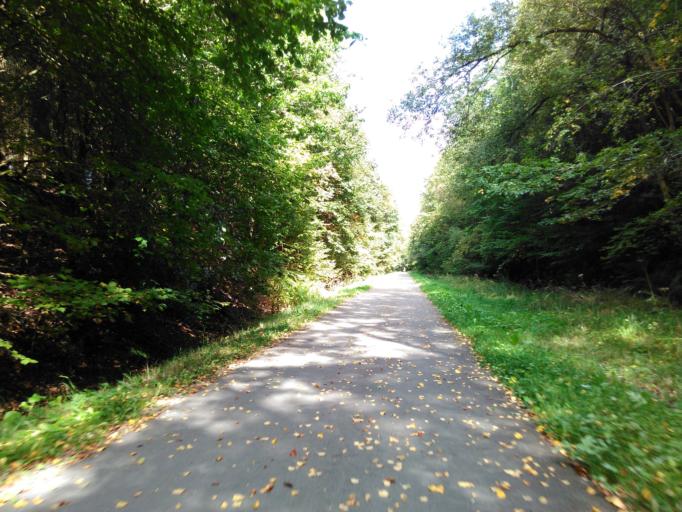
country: BE
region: Wallonia
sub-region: Province du Luxembourg
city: Gouvy
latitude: 50.1240
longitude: 5.9054
